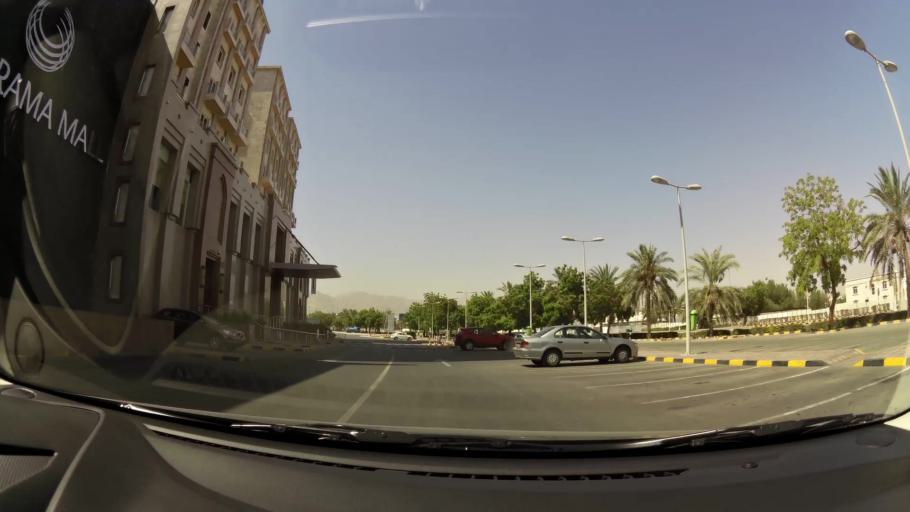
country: OM
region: Muhafazat Masqat
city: Bawshar
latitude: 23.5820
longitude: 58.4078
